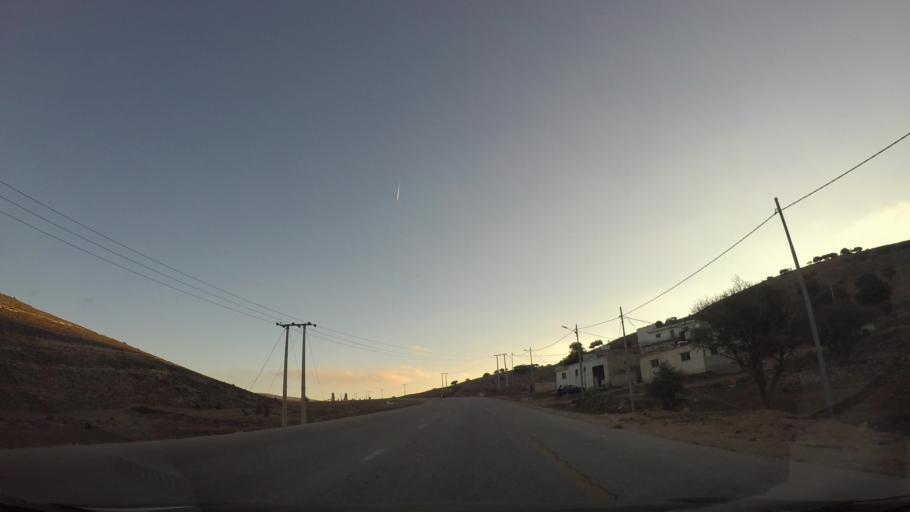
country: JO
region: Ma'an
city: Petra
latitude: 30.4080
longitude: 35.5051
